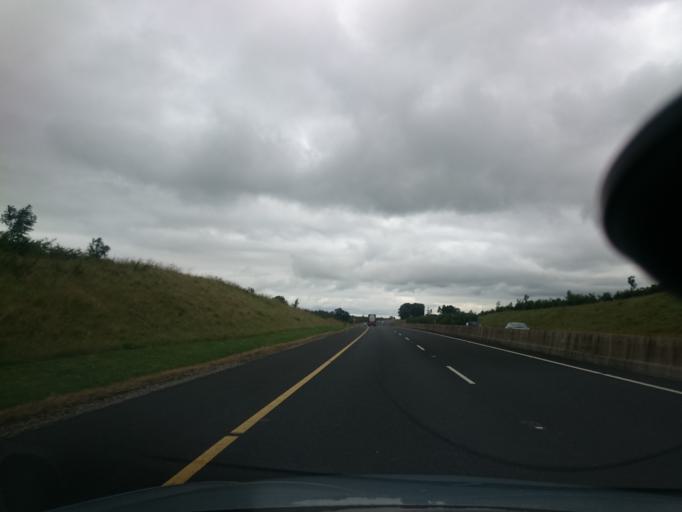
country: IE
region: Leinster
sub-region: Kildare
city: Old Kilcullen
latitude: 53.0473
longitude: -6.7895
